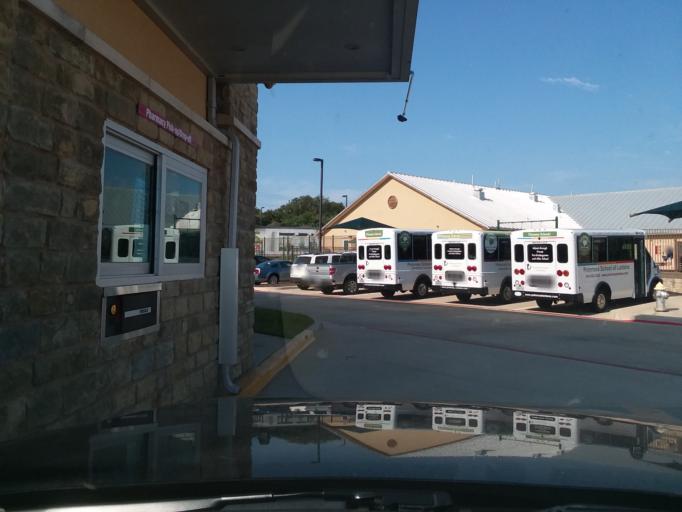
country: US
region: Texas
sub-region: Denton County
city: Double Oak
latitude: 33.0730
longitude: -97.1096
